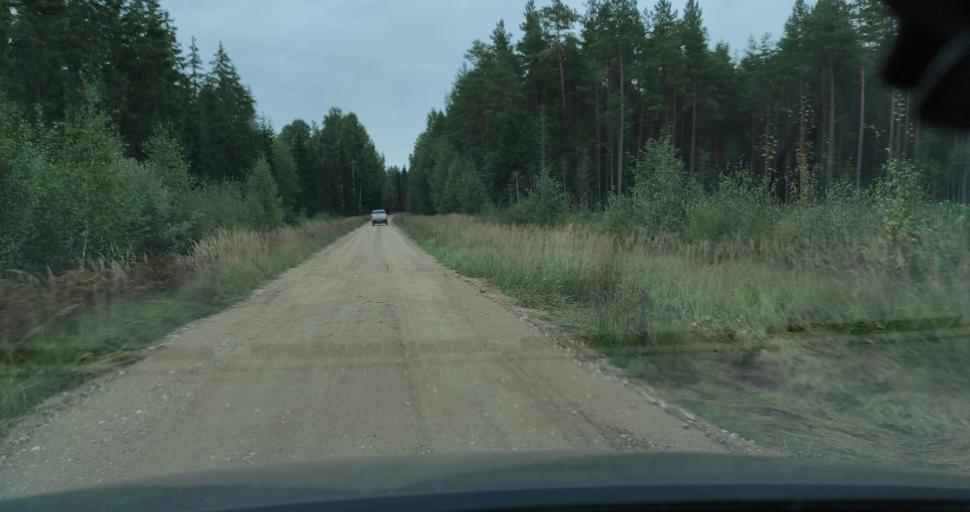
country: LV
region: Talsu Rajons
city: Stende
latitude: 57.0238
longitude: 22.3544
